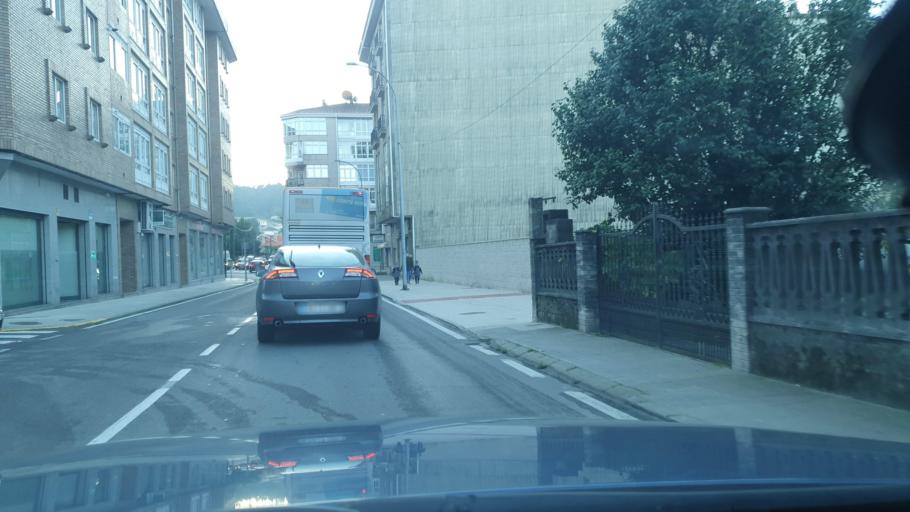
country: ES
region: Galicia
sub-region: Provincia da Coruna
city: Santiago de Compostela
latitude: 42.8424
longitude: -8.5797
